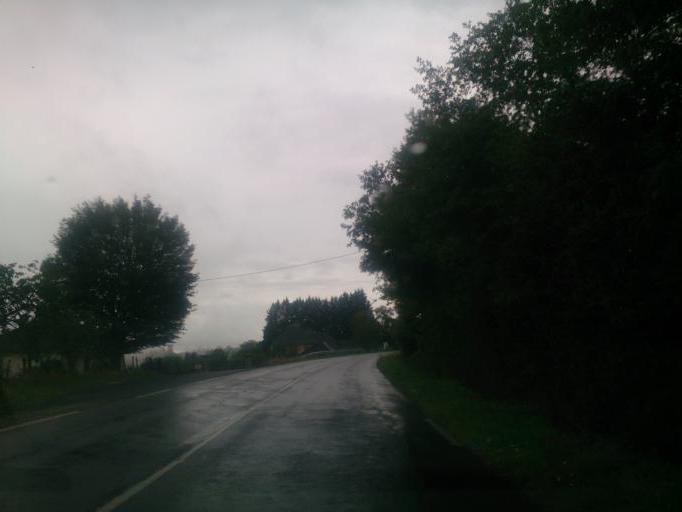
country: FR
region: Limousin
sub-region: Departement de la Correze
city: Sainte-Fereole
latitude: 45.1975
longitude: 1.5790
